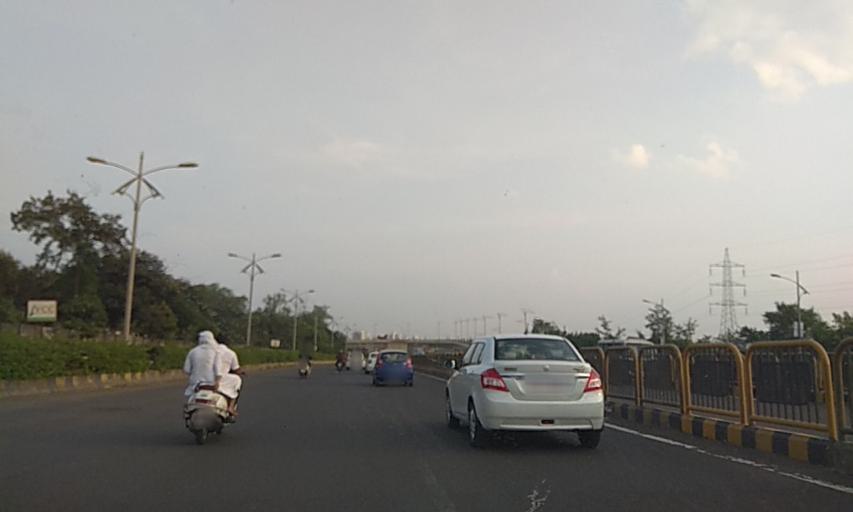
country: IN
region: Maharashtra
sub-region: Pune Division
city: Pimpri
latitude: 18.5787
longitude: 73.8015
